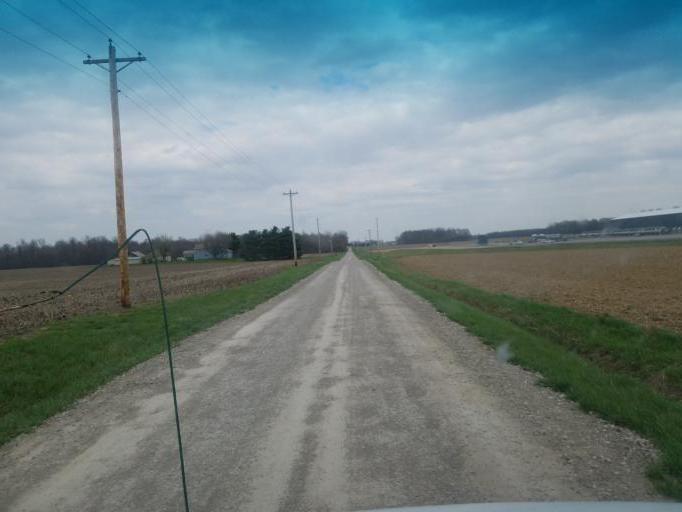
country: US
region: Ohio
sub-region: Crawford County
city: Bucyrus
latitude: 40.9793
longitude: -82.9742
